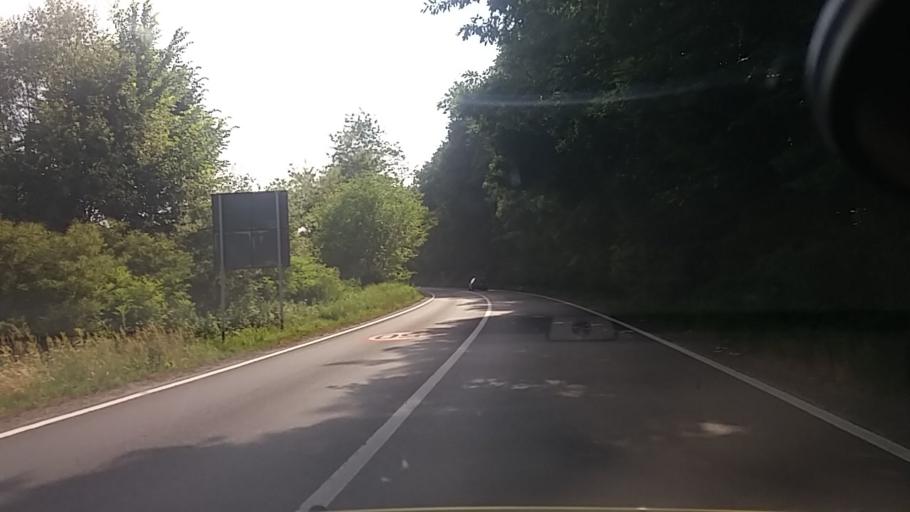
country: RO
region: Arad
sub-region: Comuna Conop
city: Conop
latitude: 46.1028
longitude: 21.9279
